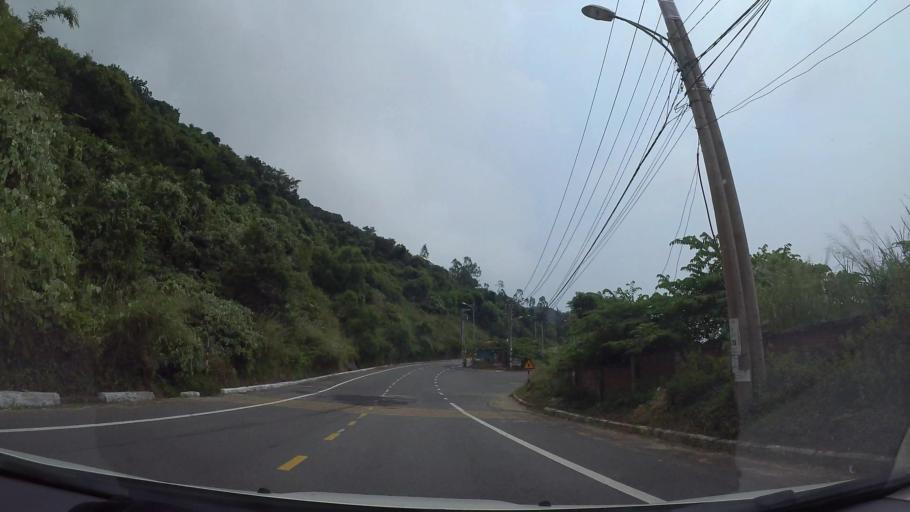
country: VN
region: Da Nang
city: Son Tra
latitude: 16.1057
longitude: 108.3000
